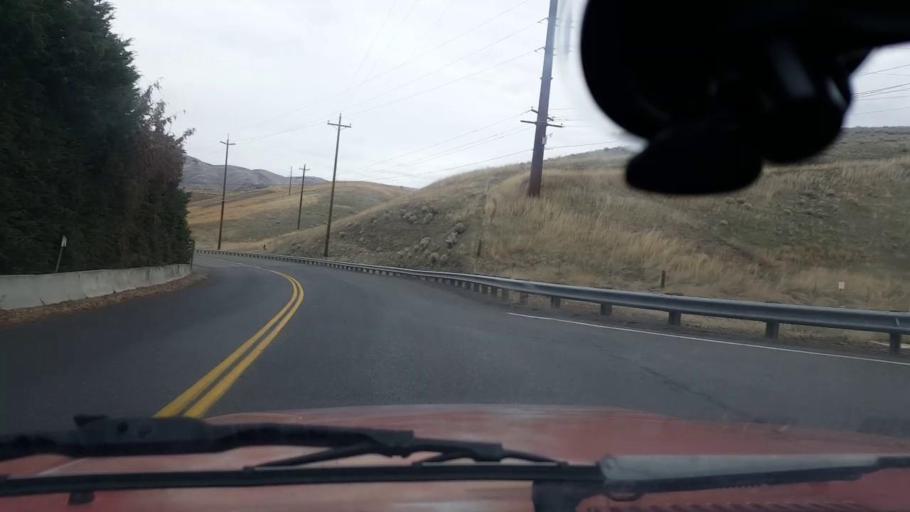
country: US
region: Washington
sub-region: Asotin County
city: Clarkston Heights-Vineland
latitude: 46.3994
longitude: -117.1010
